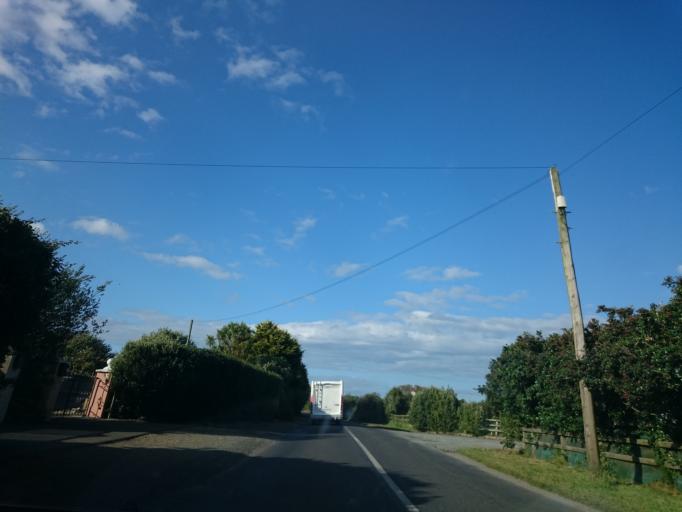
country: IE
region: Leinster
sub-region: Loch Garman
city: Loch Garman
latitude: 52.1995
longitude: -6.5552
